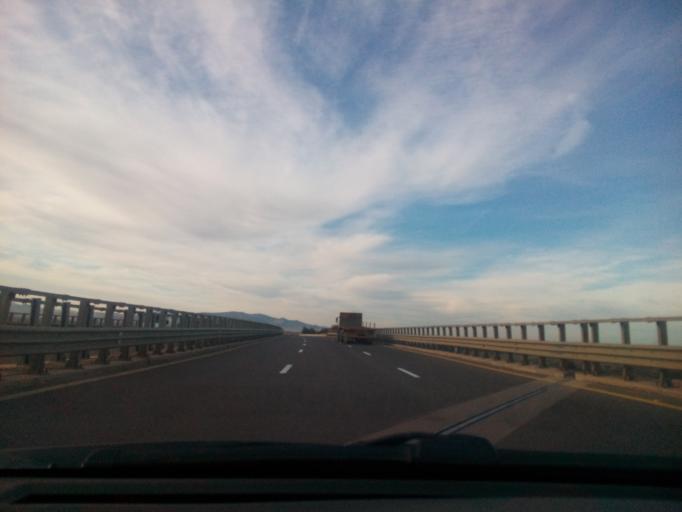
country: DZ
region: Mascara
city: Mascara
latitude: 35.6482
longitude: 0.1007
